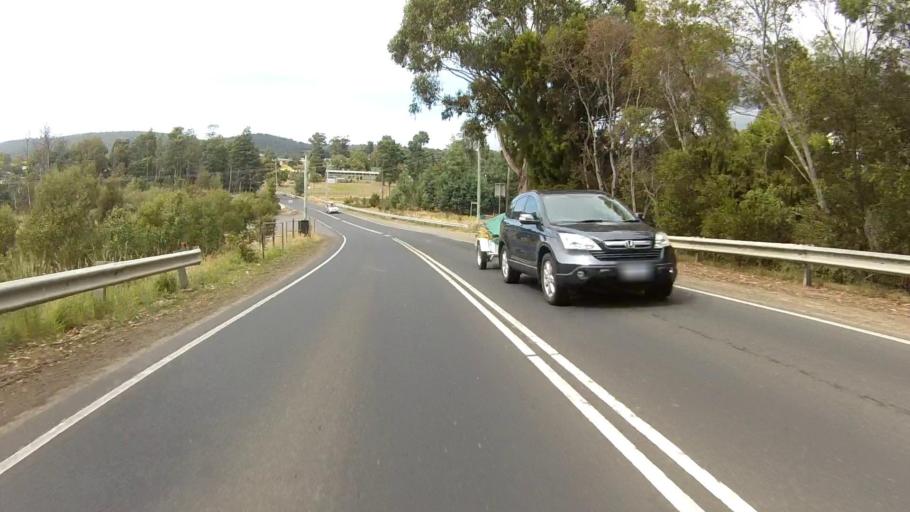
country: AU
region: Tasmania
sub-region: Kingborough
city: Margate
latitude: -43.0626
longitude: 147.2535
